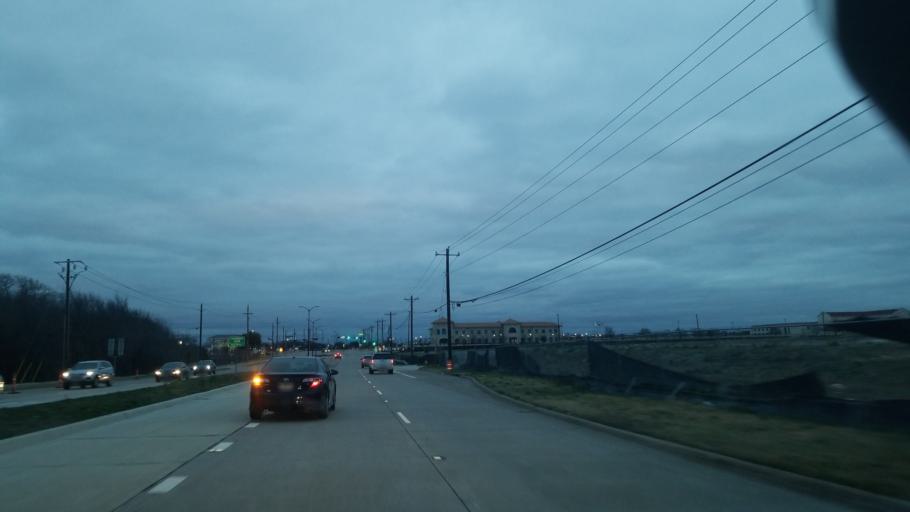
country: US
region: Texas
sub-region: Collin County
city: Frisco
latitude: 33.1236
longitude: -96.8196
